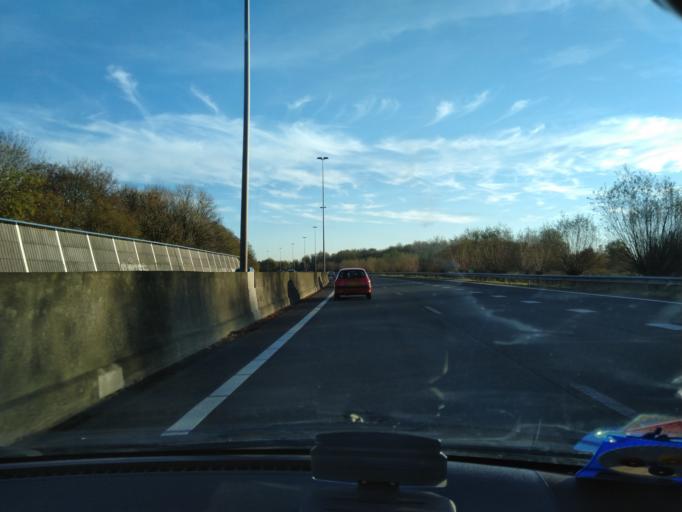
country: NL
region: Groningen
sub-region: Gemeente Groningen
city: Groningen
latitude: 53.1890
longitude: 6.5664
